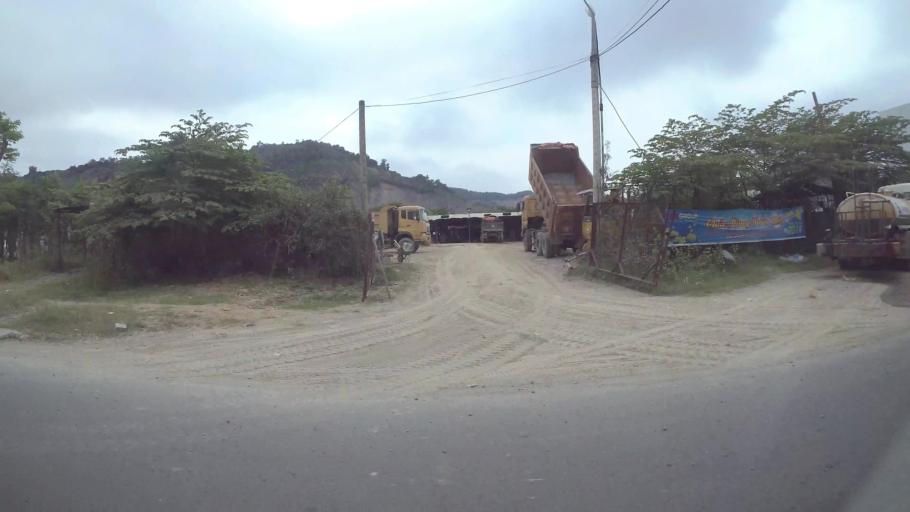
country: VN
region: Da Nang
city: Lien Chieu
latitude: 16.0447
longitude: 108.1664
